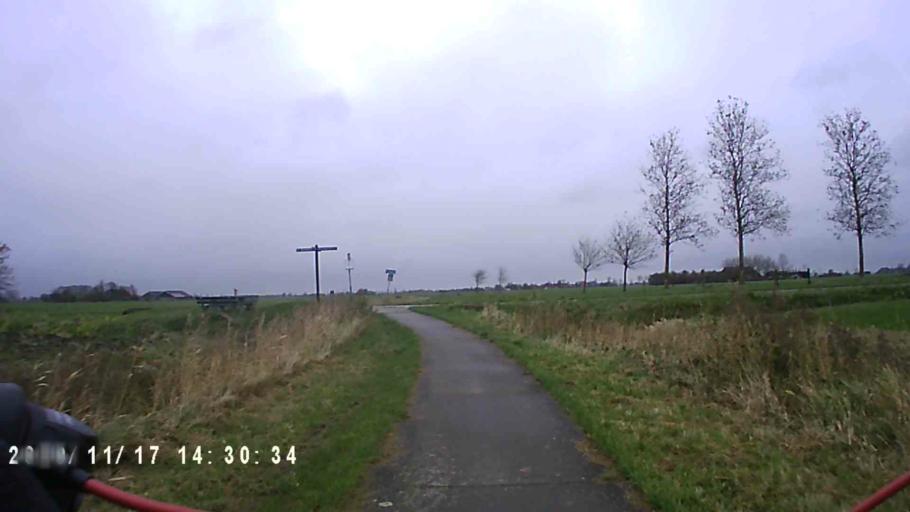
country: NL
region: Groningen
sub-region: Gemeente Zuidhorn
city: Noordhorn
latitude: 53.2785
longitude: 6.3540
